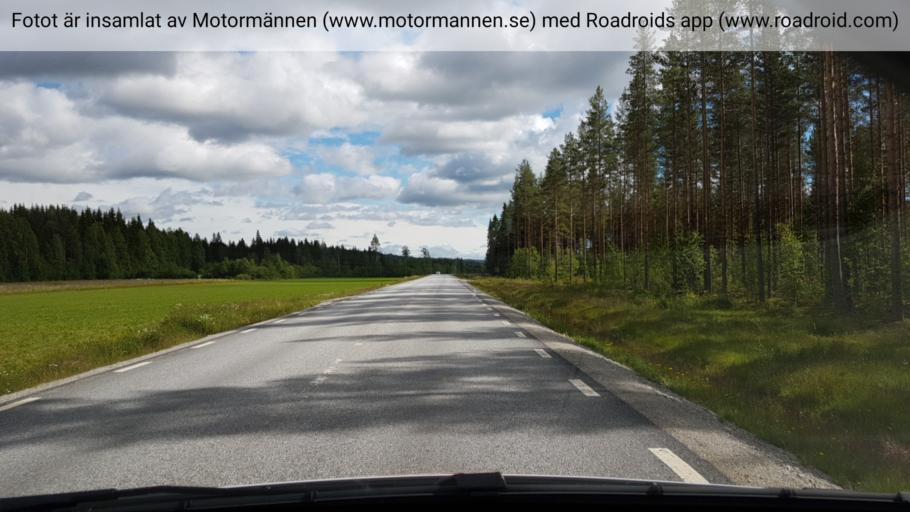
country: SE
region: Vaesterbotten
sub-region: Vindelns Kommun
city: Vindeln
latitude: 64.2009
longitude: 19.4466
